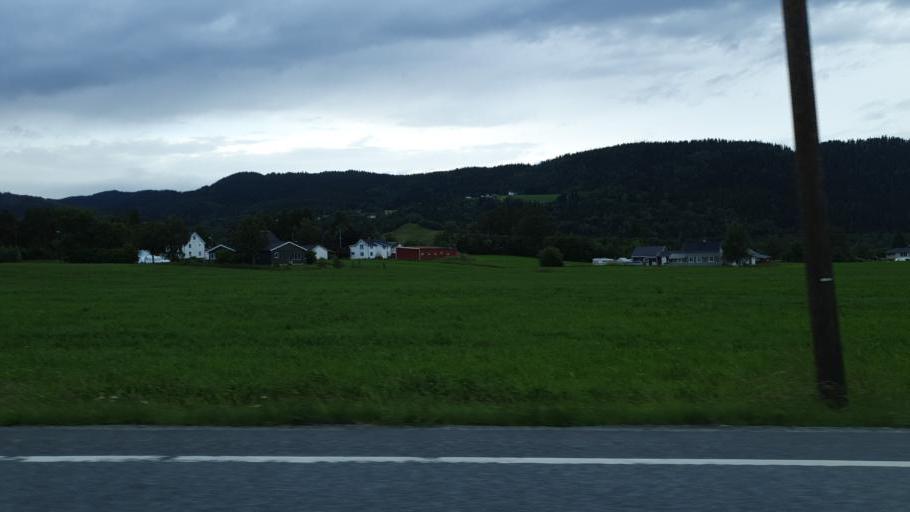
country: NO
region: Sor-Trondelag
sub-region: Melhus
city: Lundamo
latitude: 63.1778
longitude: 10.3168
